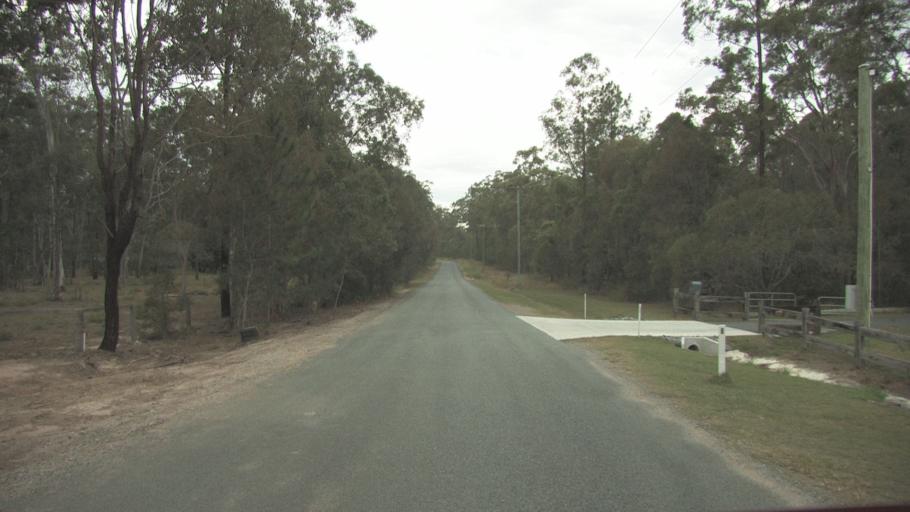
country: AU
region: Queensland
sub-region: Logan
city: Chambers Flat
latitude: -27.7938
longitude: 153.1184
